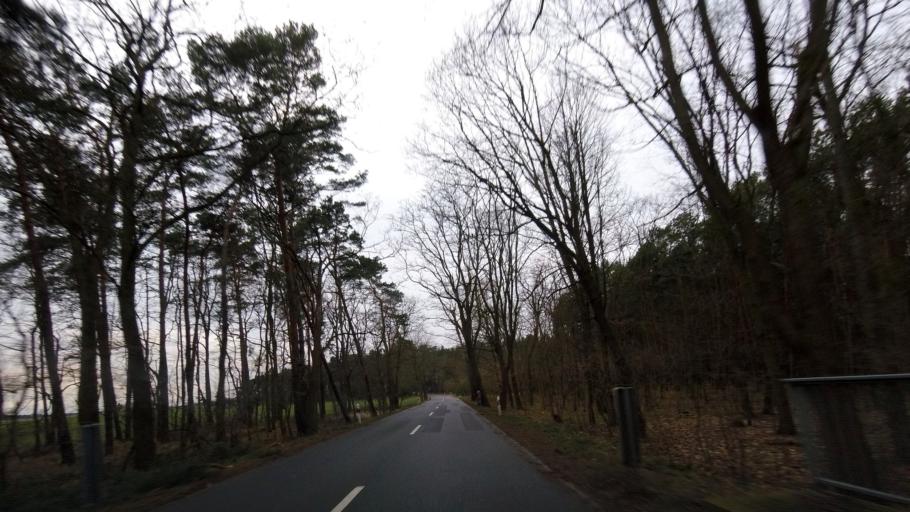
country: DE
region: Saxony-Anhalt
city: Seyda
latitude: 51.9236
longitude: 12.9537
